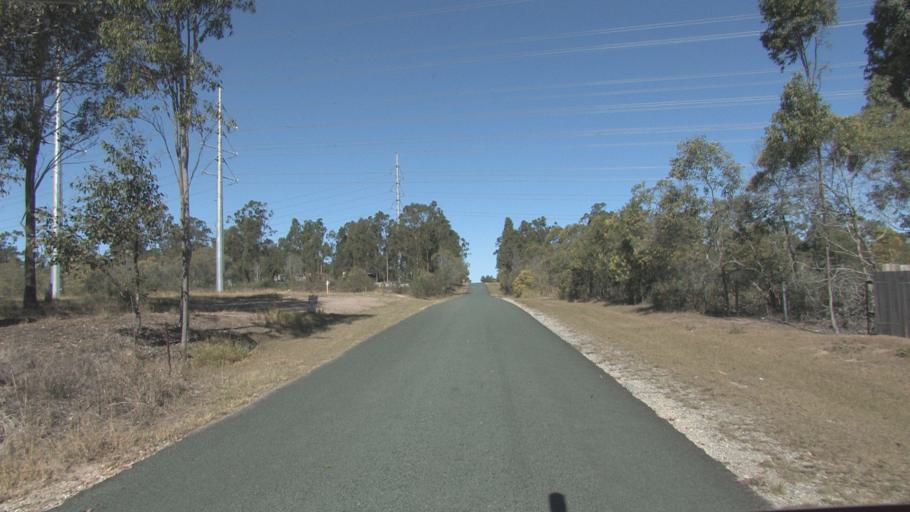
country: AU
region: Queensland
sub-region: Ipswich
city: Springfield Lakes
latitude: -27.7175
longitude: 152.9303
